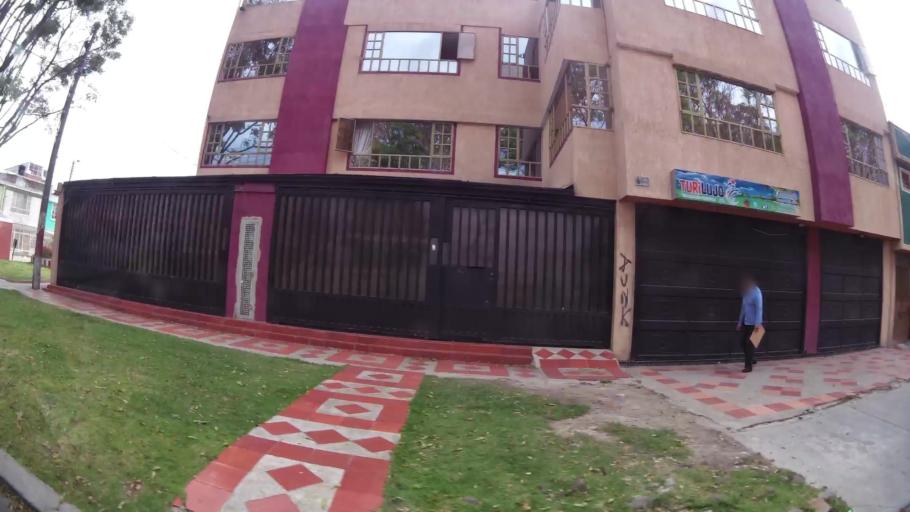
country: CO
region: Bogota D.C.
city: Bogota
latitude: 4.6008
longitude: -74.1298
